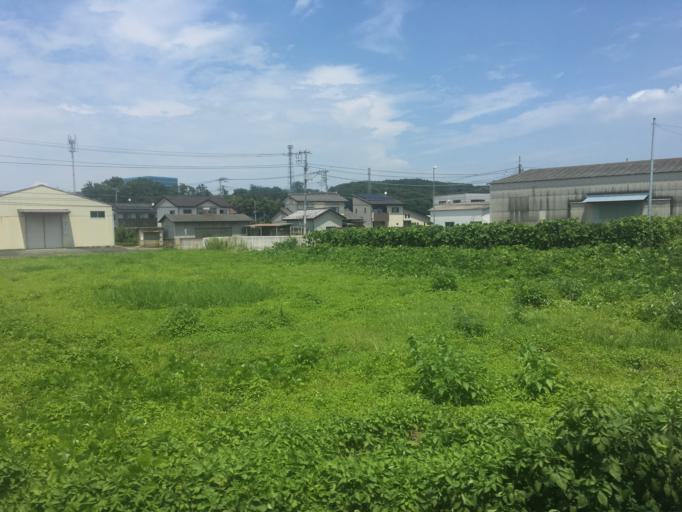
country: JP
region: Saitama
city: Kodamacho-kodamaminami
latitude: 36.1895
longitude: 139.1389
